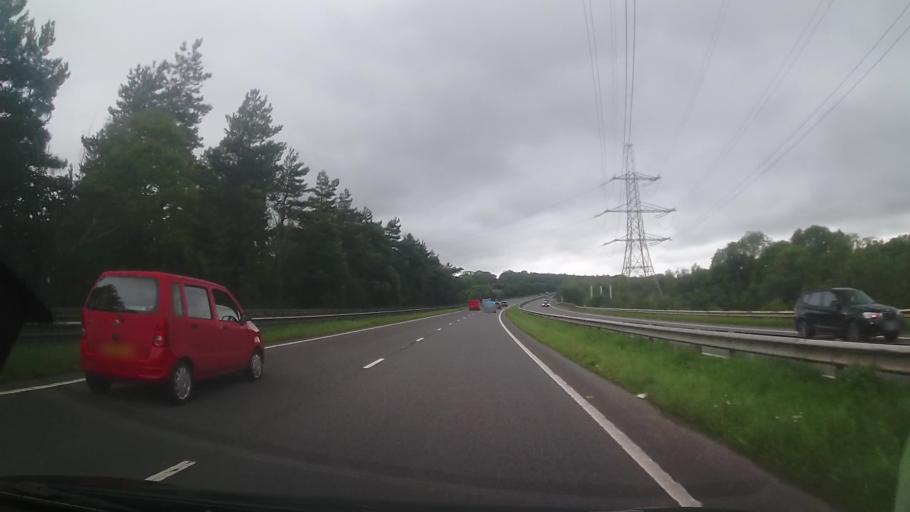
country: GB
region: Wales
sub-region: Gwynedd
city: Bangor
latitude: 53.2004
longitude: -4.1161
